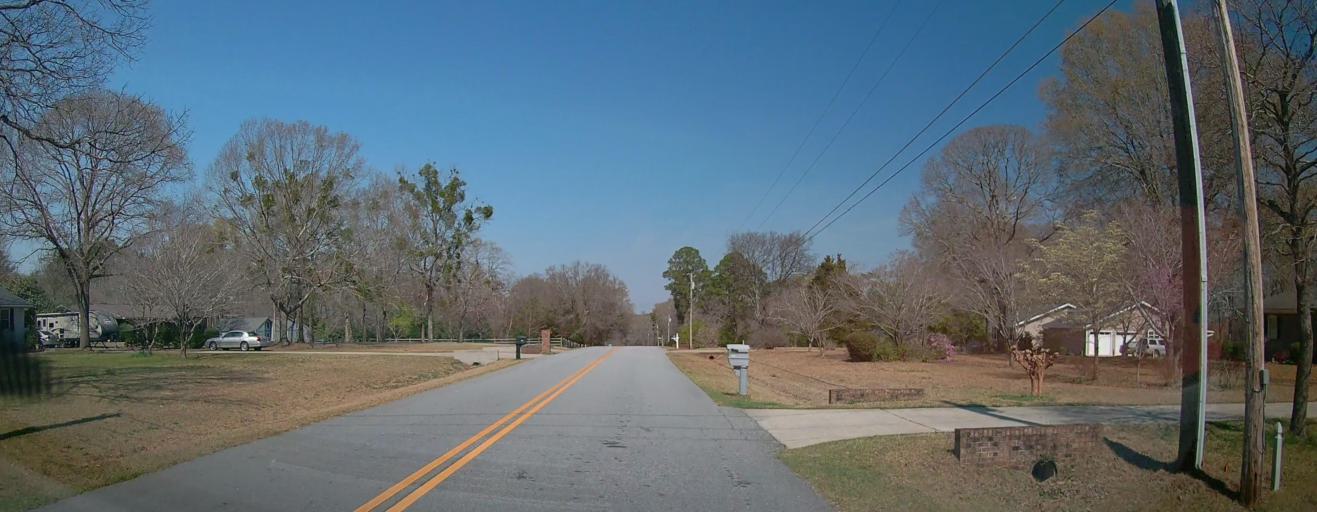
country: US
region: Georgia
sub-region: Houston County
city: Centerville
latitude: 32.5889
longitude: -83.6916
